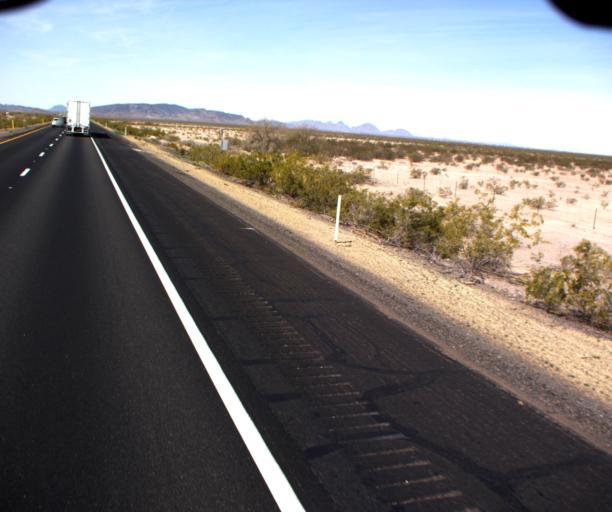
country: US
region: Arizona
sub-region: La Paz County
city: Salome
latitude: 33.6347
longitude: -113.7907
